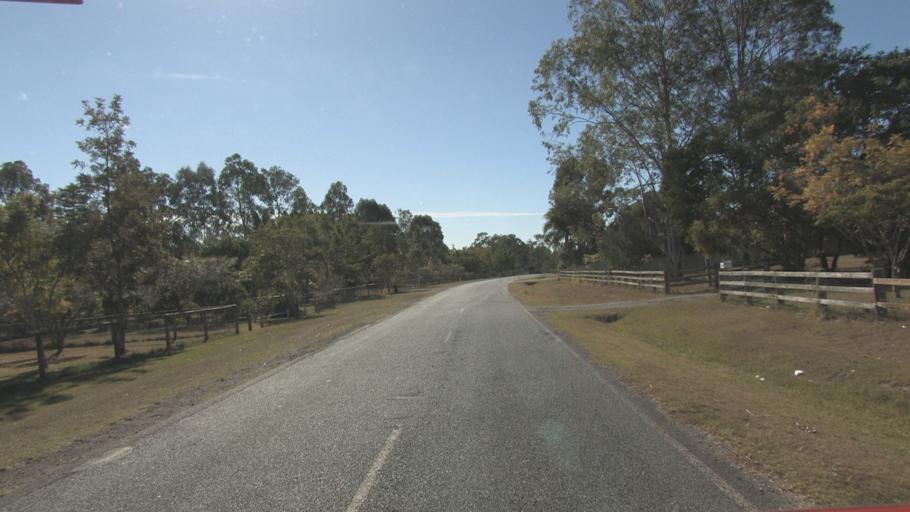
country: AU
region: Queensland
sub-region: Logan
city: North Maclean
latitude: -27.8253
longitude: 152.9482
